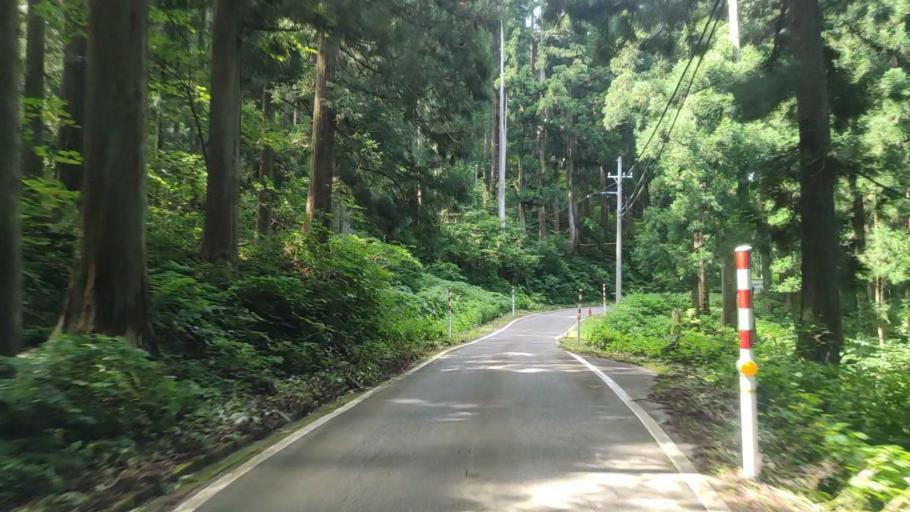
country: JP
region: Fukui
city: Katsuyama
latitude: 36.2209
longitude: 136.5315
